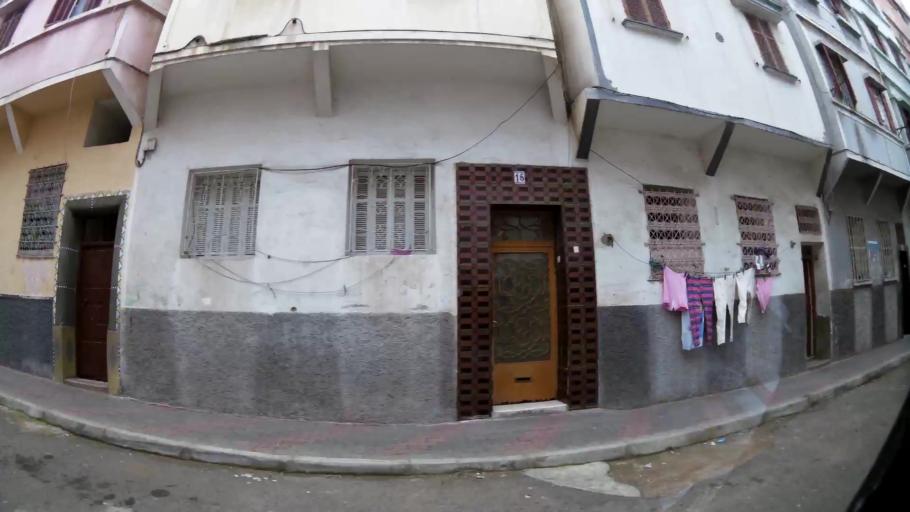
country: MA
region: Grand Casablanca
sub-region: Casablanca
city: Casablanca
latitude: 33.5825
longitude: -7.5654
